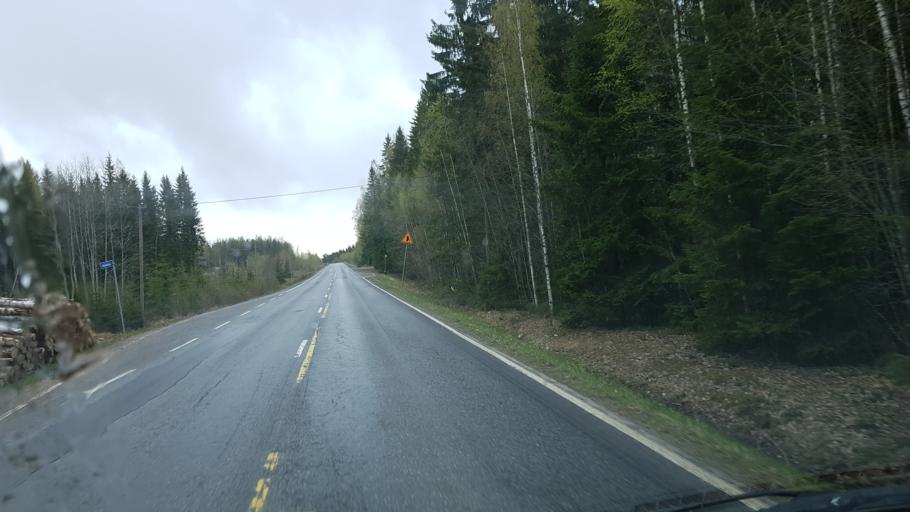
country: FI
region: Pirkanmaa
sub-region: Tampere
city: Pirkkala
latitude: 61.4006
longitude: 23.6298
